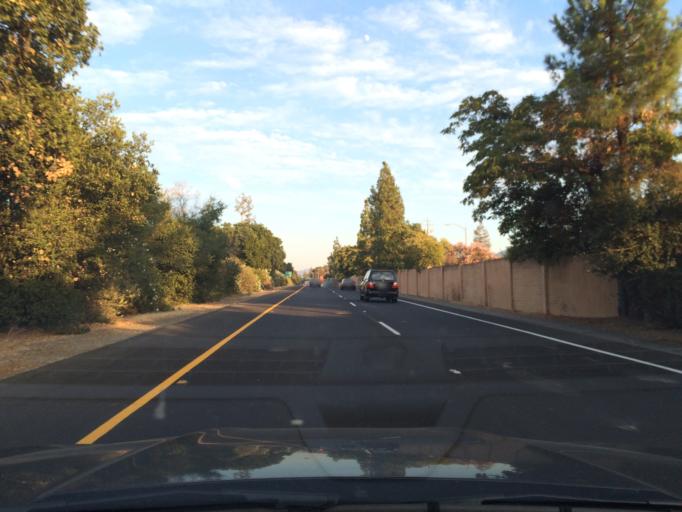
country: US
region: California
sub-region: Santa Clara County
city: Seven Trees
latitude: 37.2239
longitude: -121.8655
